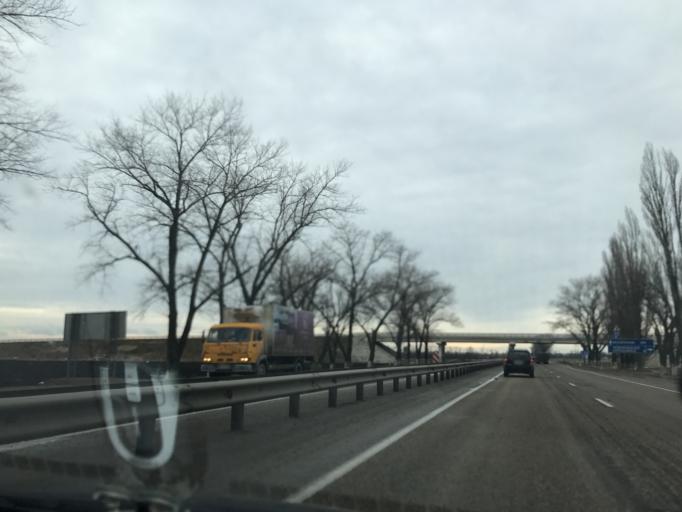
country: RU
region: Krasnodarskiy
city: Novokubansk
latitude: 45.0606
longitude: 40.9828
